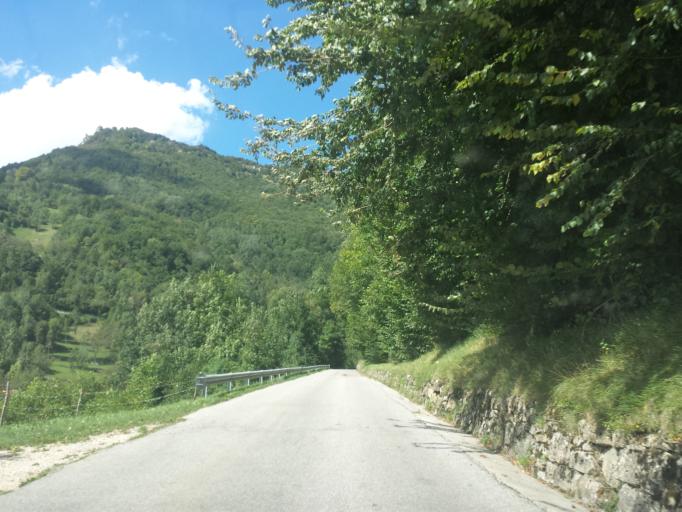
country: IT
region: Veneto
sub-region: Provincia di Vicenza
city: Recoaro Terme
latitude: 45.7173
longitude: 11.1974
